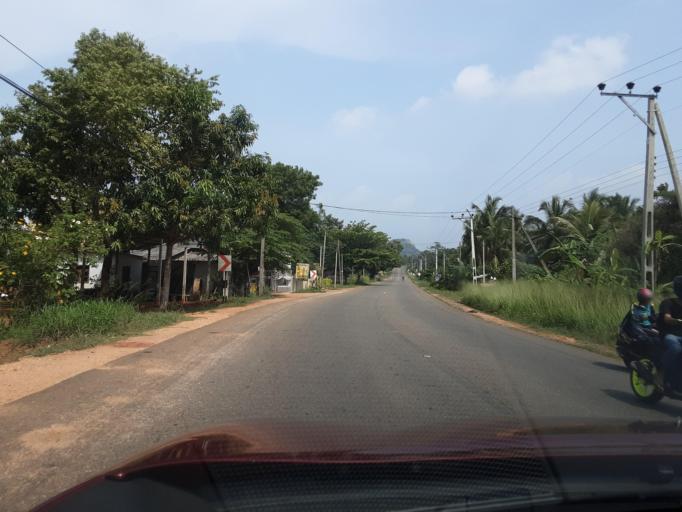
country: LK
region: North Central
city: Anuradhapura
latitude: 8.3351
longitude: 80.5012
